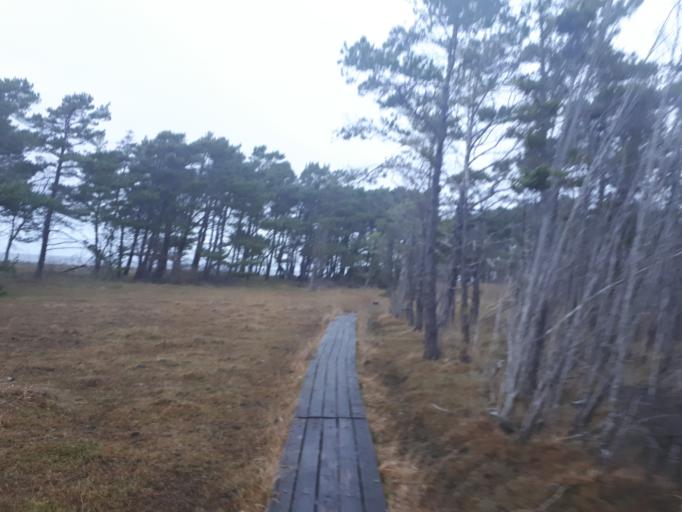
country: SE
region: Gotland
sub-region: Gotland
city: Visby
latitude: 57.6869
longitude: 18.3464
